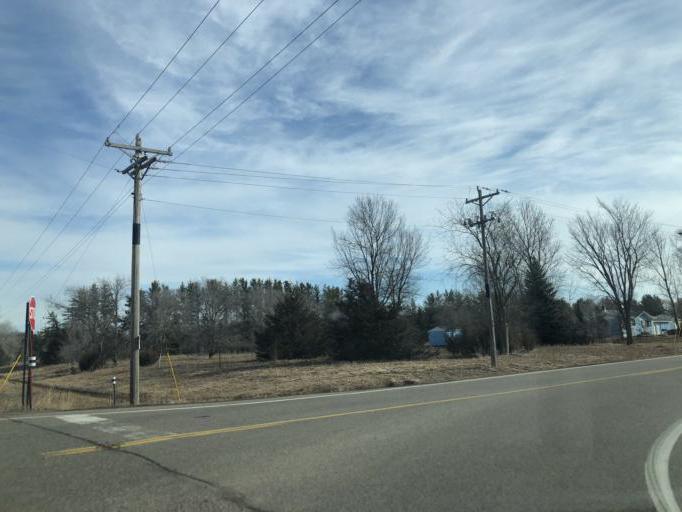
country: US
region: Minnesota
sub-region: Sherburne County
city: Becker
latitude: 45.4297
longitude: -93.8763
